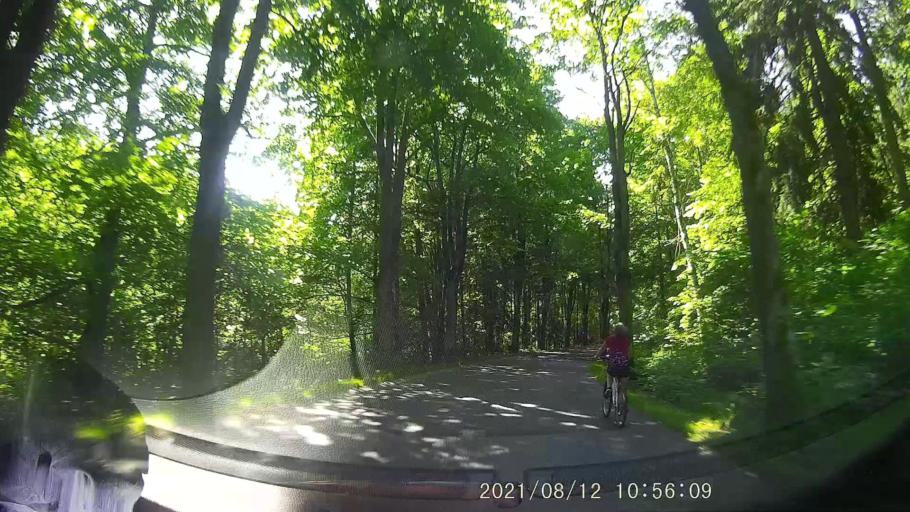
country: PL
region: Lower Silesian Voivodeship
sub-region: Powiat klodzki
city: Polanica-Zdroj
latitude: 50.4027
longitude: 16.4855
